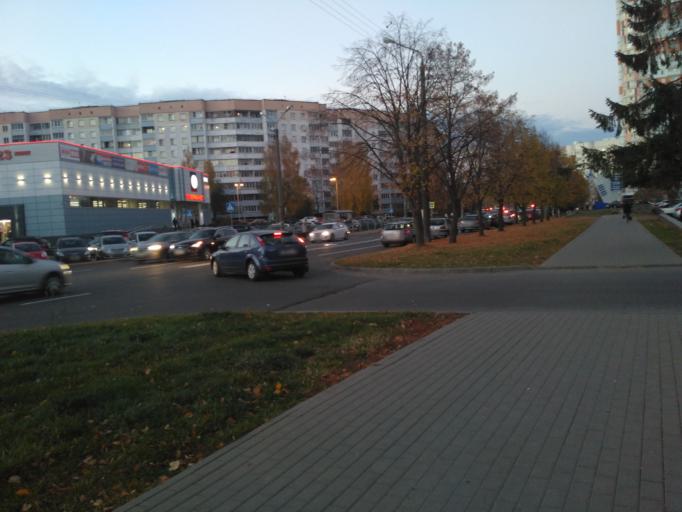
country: BY
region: Minsk
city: Novoye Medvezhino
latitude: 53.8675
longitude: 27.4851
